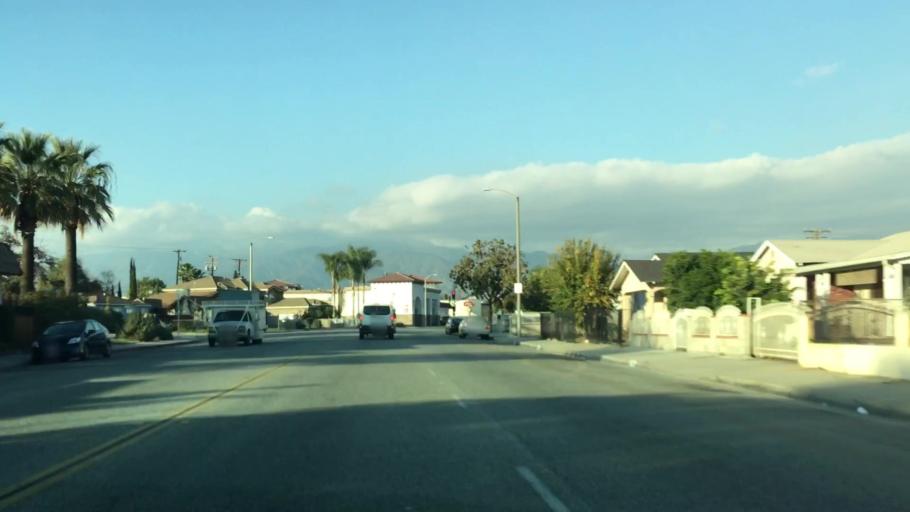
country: US
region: California
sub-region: Los Angeles County
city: Rosemead
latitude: 34.0779
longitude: -118.0586
